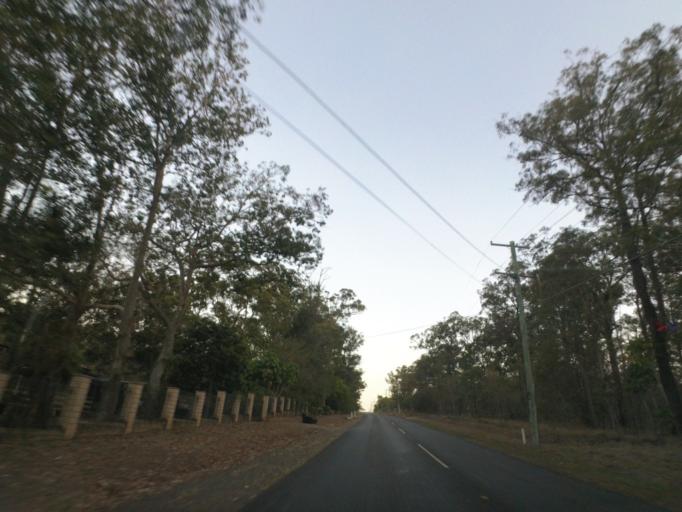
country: AU
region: Queensland
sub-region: Brisbane
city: Mackenzie
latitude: -27.5501
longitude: 153.1267
